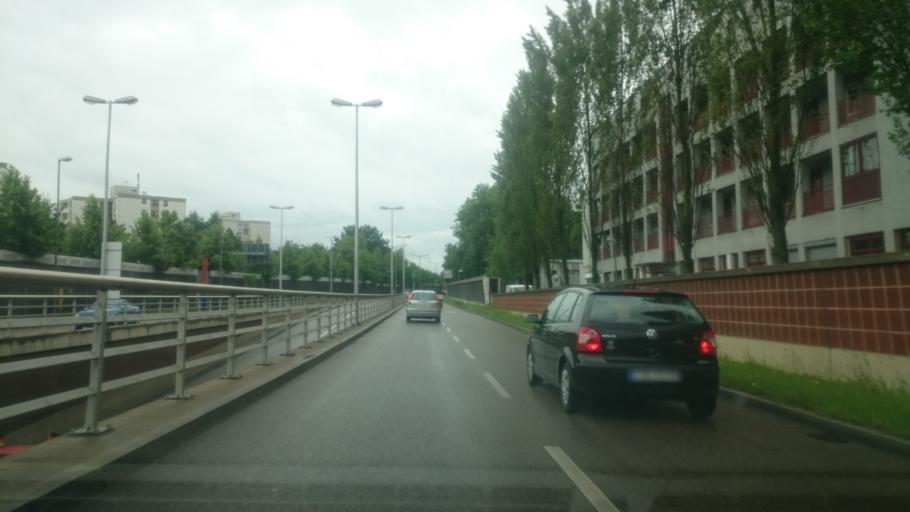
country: DE
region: Bavaria
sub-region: Swabia
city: Augsburg
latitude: 48.3751
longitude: 10.9278
